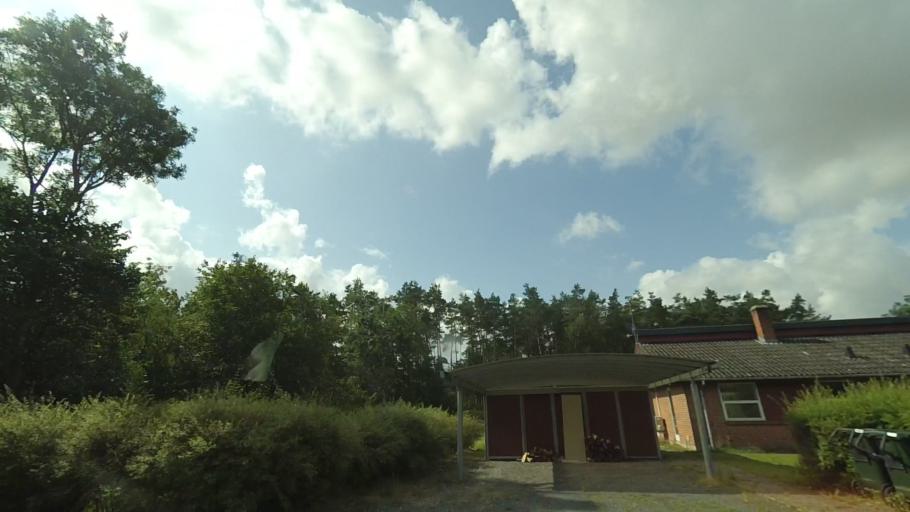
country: DK
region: Central Jutland
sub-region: Norddjurs Kommune
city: Allingabro
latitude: 56.5138
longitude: 10.3964
